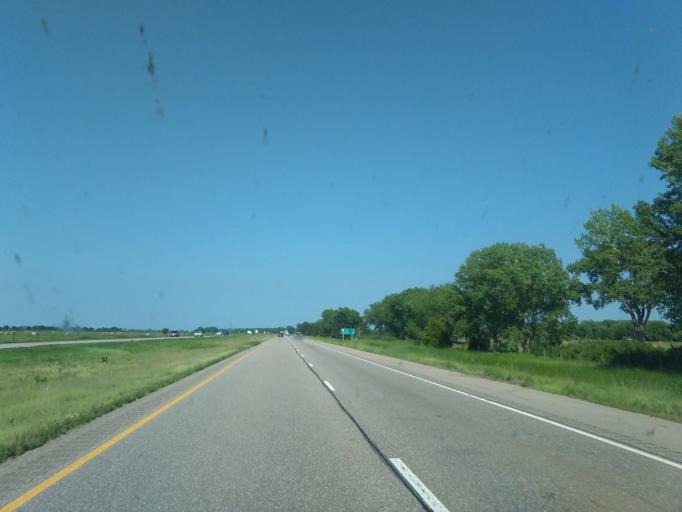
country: US
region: Nebraska
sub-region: Hall County
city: Wood River
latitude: 40.7664
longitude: -98.5754
